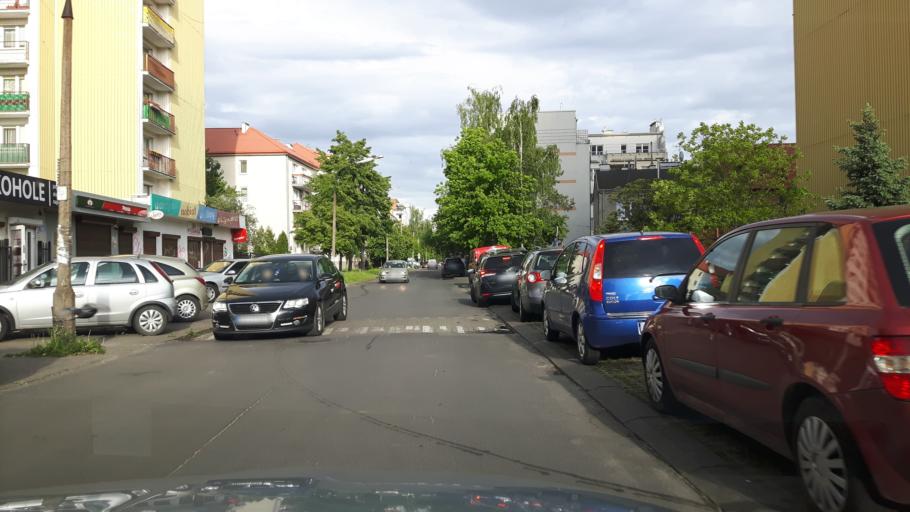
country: PL
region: Masovian Voivodeship
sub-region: Warszawa
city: Praga Poludnie
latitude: 52.2464
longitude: 21.0973
